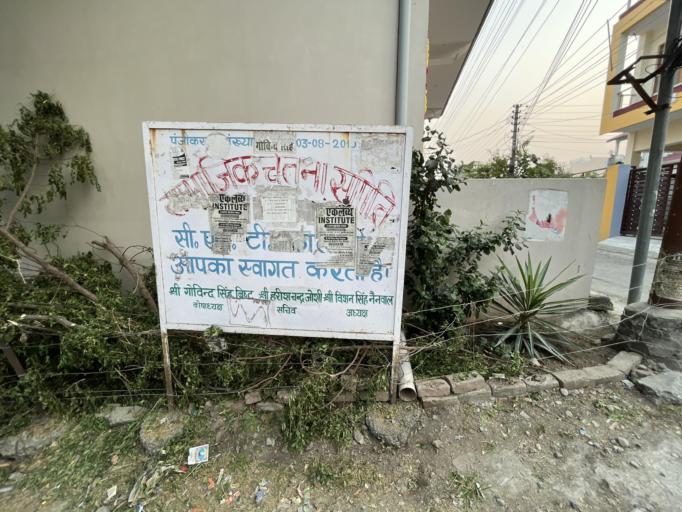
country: IN
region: Uttarakhand
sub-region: Naini Tal
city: Haldwani
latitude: 29.2010
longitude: 79.5120
